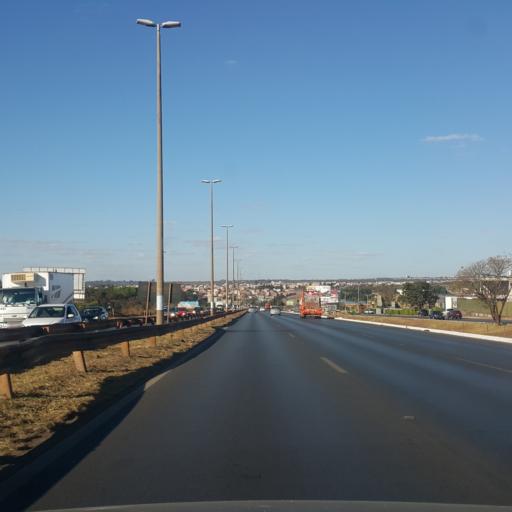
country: BR
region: Federal District
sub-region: Brasilia
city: Brasilia
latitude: -15.7886
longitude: -48.0154
